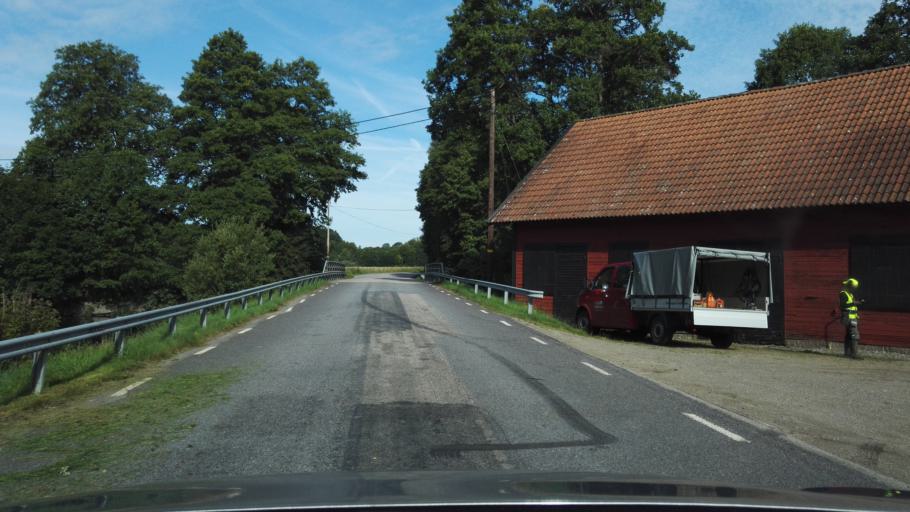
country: SE
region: Kronoberg
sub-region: Vaxjo Kommun
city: Vaexjoe
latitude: 56.8681
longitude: 14.7337
